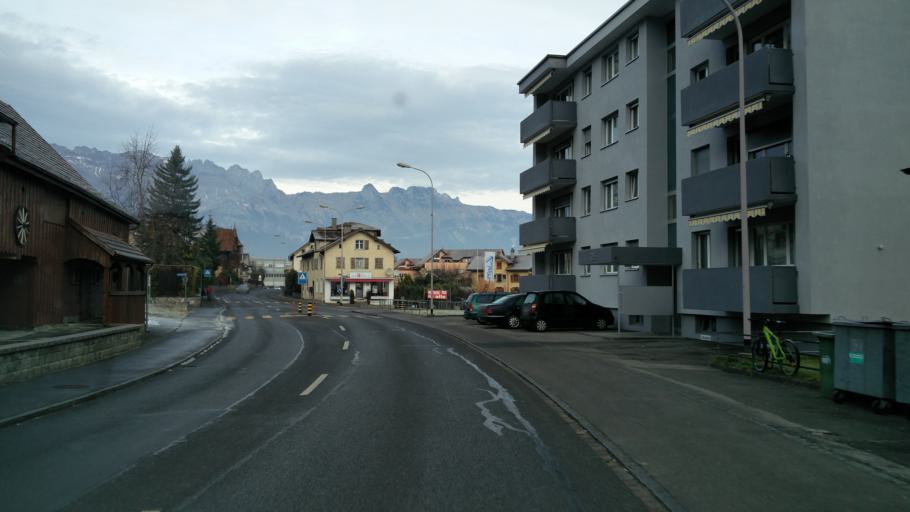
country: CH
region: Saint Gallen
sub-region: Wahlkreis Werdenberg
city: Buchs
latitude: 47.1612
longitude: 9.4759
